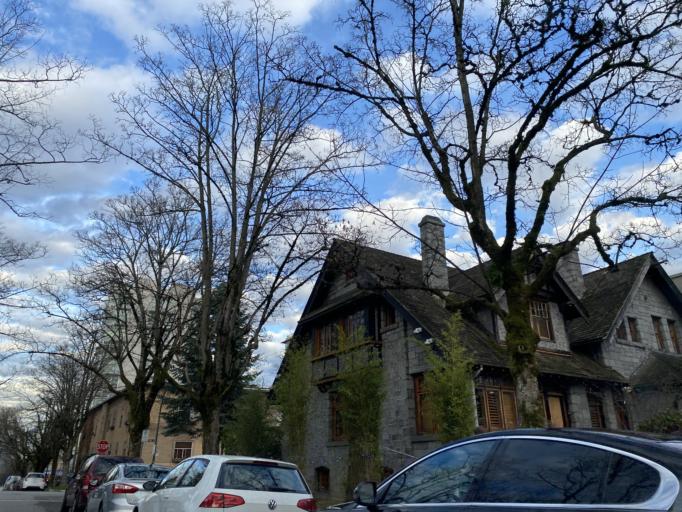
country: CA
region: British Columbia
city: Vancouver
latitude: 49.2620
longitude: -123.1291
